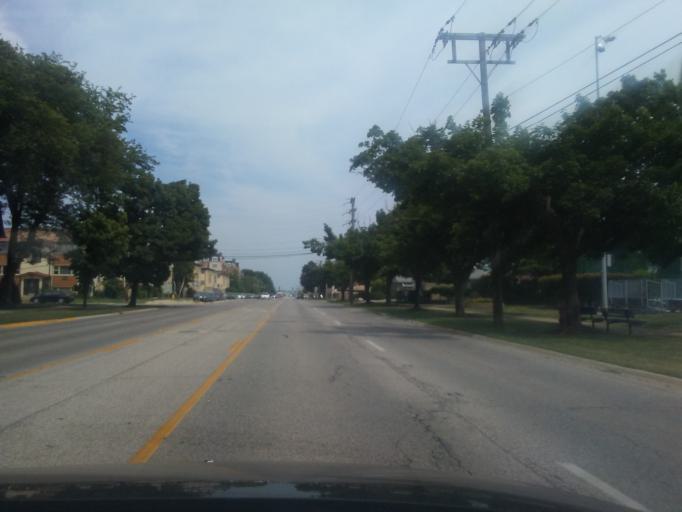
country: US
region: Illinois
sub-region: Cook County
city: Harwood Heights
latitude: 41.9670
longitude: -87.8177
